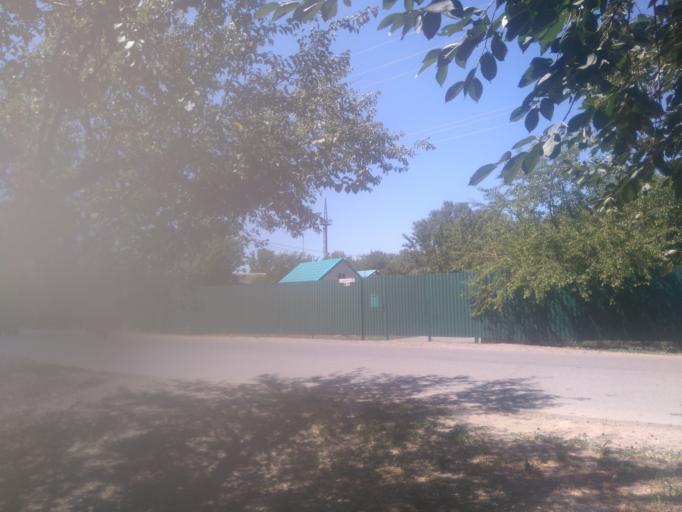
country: RU
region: Krasnodarskiy
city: Fastovetskaya
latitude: 45.9135
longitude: 40.1543
